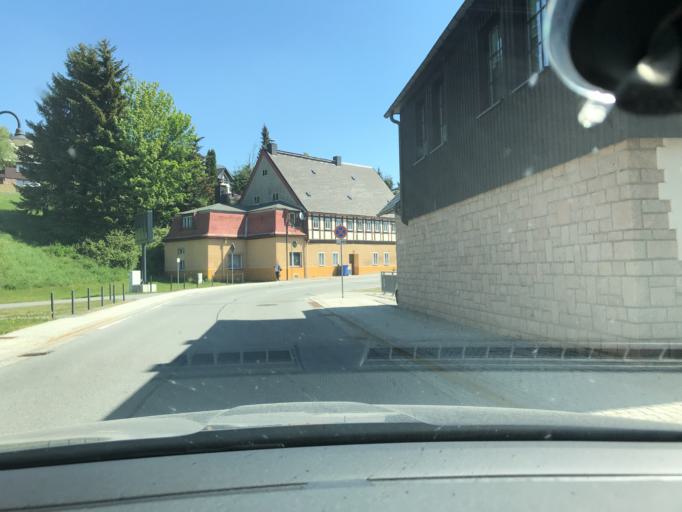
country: DE
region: Saxony
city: Kurort Oberwiesenthal
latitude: 50.4198
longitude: 12.9797
